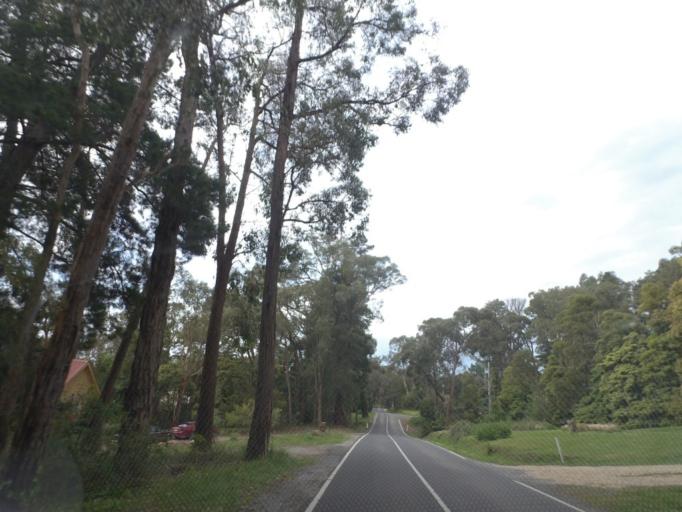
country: AU
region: Victoria
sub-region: Yarra Ranges
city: Montrose
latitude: -37.8176
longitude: 145.3478
